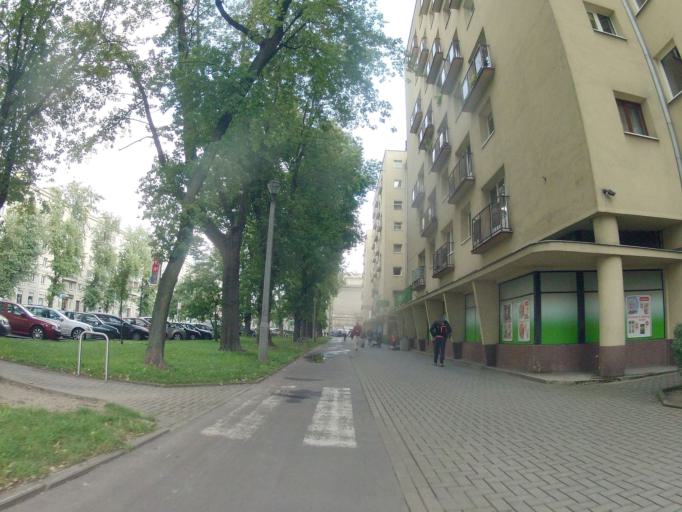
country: PL
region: Lesser Poland Voivodeship
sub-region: Powiat wielicki
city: Kokotow
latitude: 50.0743
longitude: 20.0340
